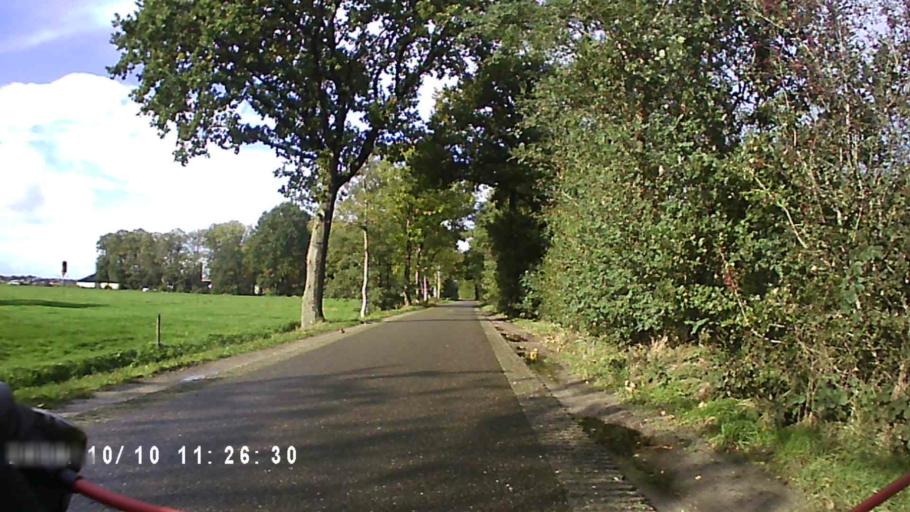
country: NL
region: Friesland
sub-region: Gemeente Smallingerland
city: Drachtstercompagnie
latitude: 53.0878
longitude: 6.1640
